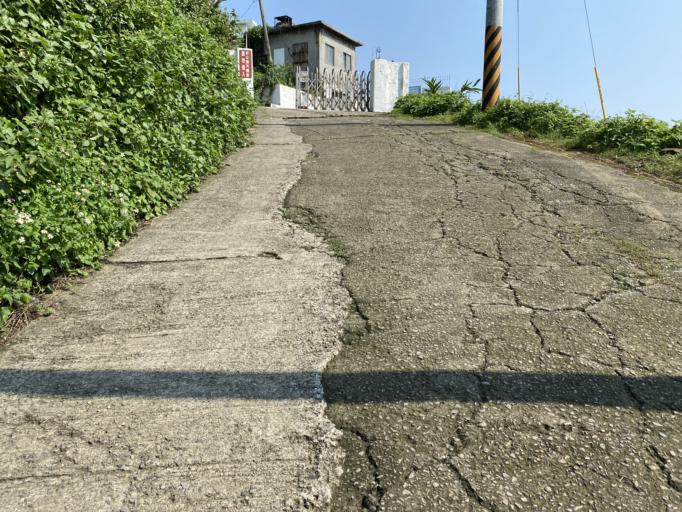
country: TW
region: Taiwan
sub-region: Keelung
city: Keelung
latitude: 25.1547
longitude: 121.7473
